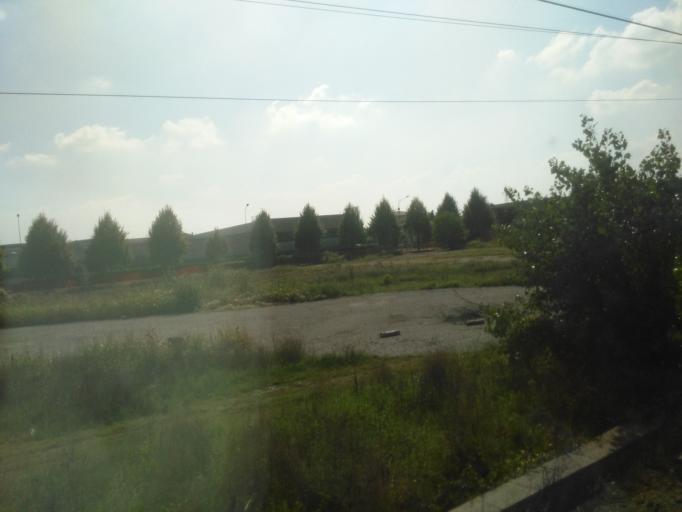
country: IT
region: Lombardy
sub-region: Provincia di Bergamo
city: Casirate d'Adda
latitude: 45.5140
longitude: 9.5722
